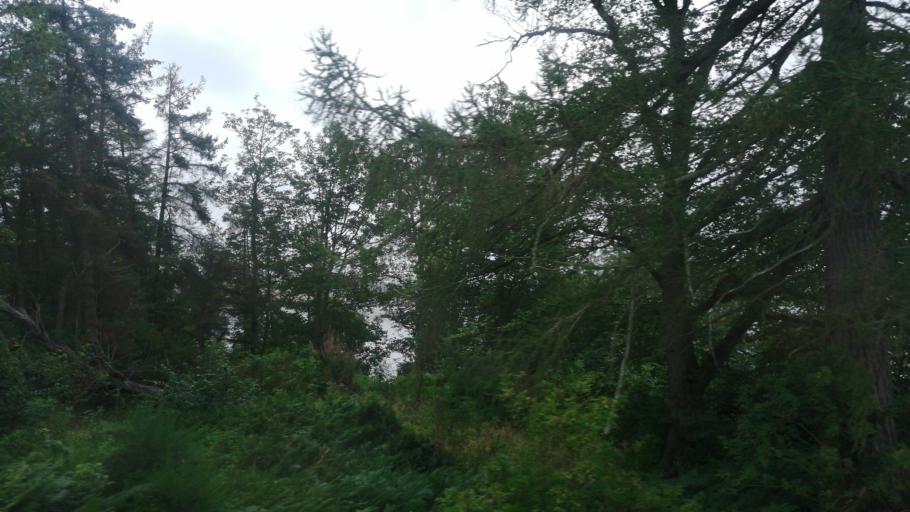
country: GB
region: Scotland
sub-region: Highland
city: Evanton
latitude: 57.6320
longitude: -4.3667
